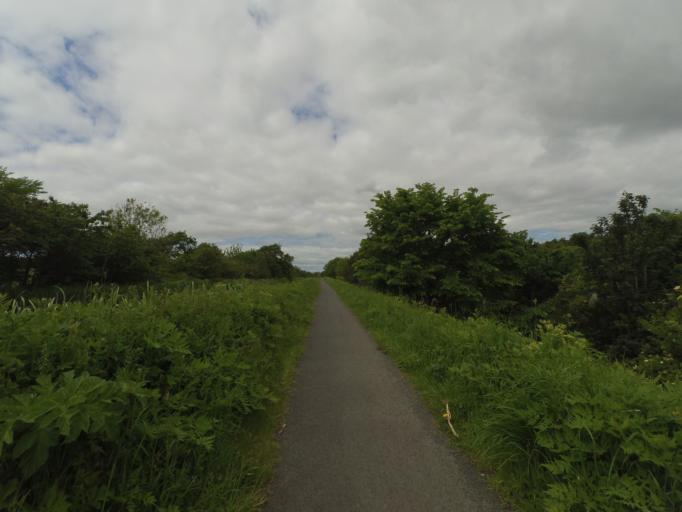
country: GB
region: Scotland
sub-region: Falkirk
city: Polmont
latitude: 55.9760
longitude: -3.6767
